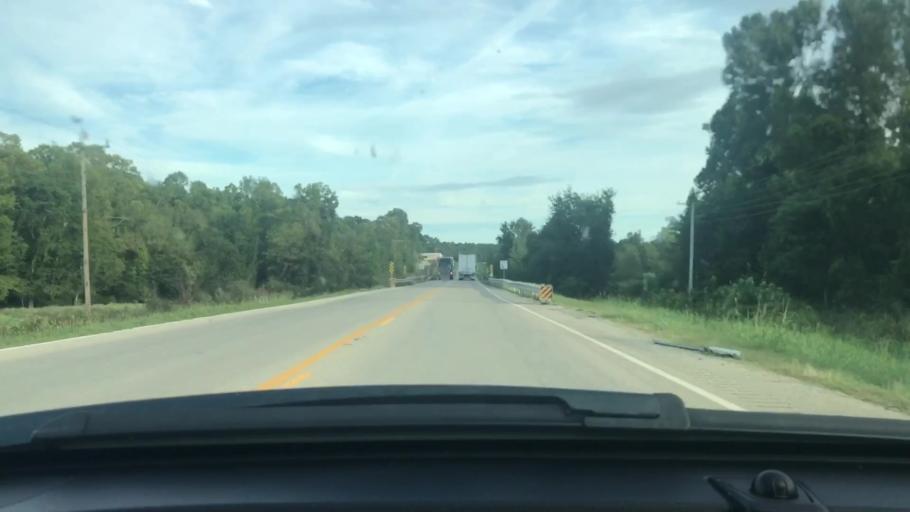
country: US
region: Arkansas
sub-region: Lawrence County
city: Hoxie
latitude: 36.1218
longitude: -91.1497
